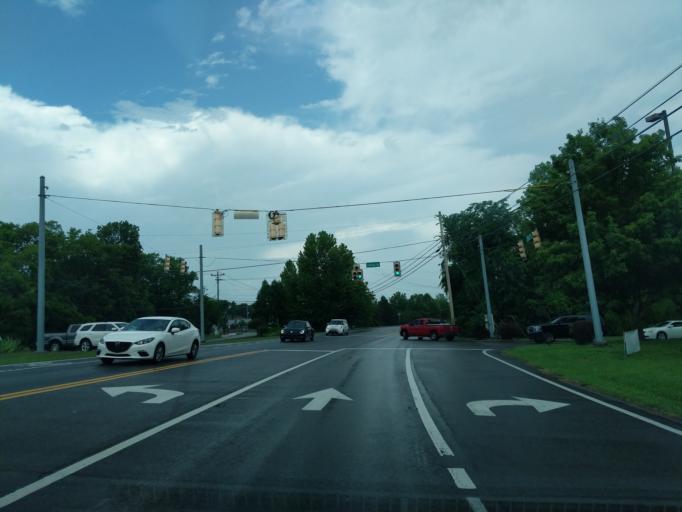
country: US
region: Tennessee
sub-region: Cheatham County
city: Pegram
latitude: 36.0435
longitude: -86.9591
